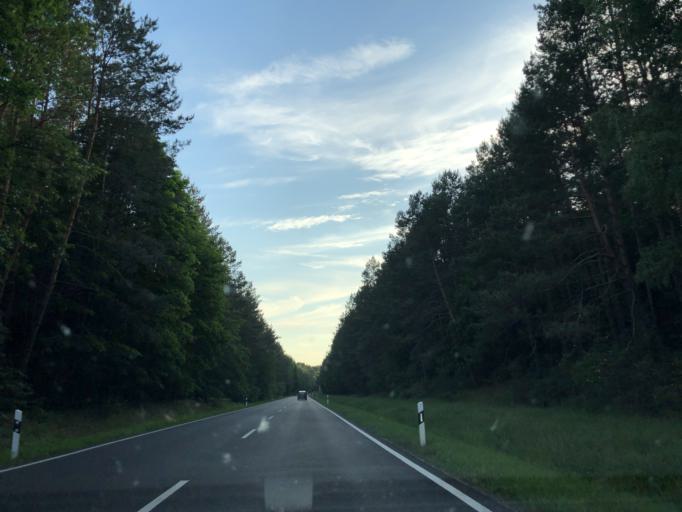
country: DE
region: Brandenburg
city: Wandlitz
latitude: 52.7283
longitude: 13.5177
